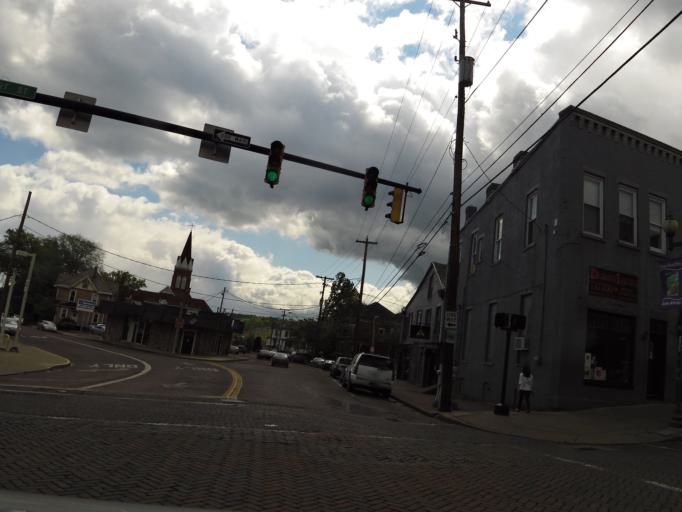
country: US
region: Ohio
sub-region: Athens County
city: Athens
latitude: 39.3306
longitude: -82.1011
